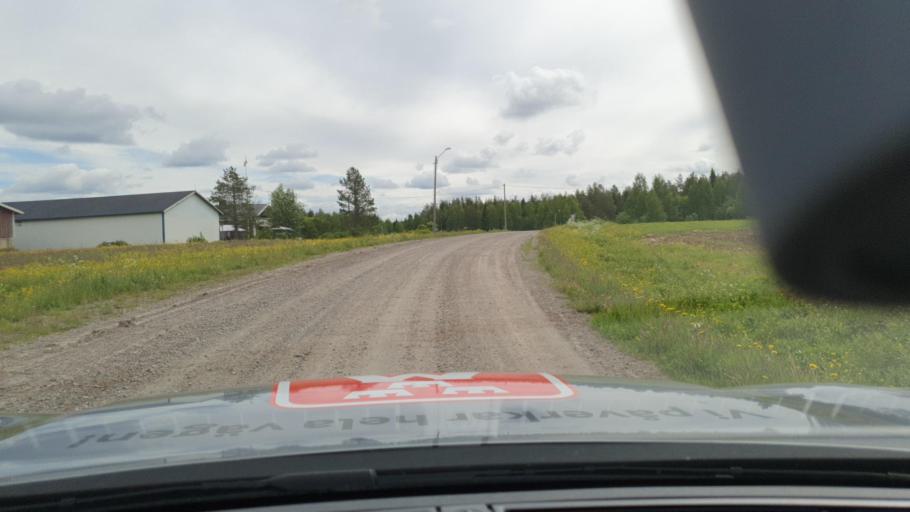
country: FI
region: Lapland
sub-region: Torniolaakso
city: Ylitornio
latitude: 65.9636
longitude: 23.6746
